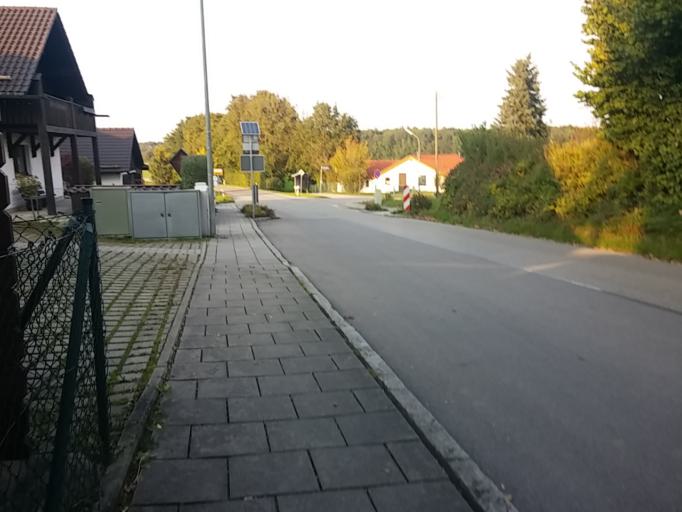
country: DE
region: Bavaria
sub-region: Upper Bavaria
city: Zorneding
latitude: 48.0966
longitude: 11.8331
